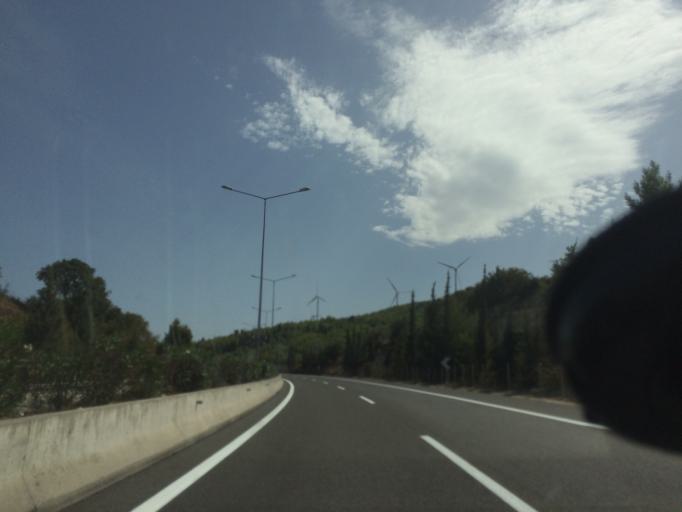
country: GR
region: Central Greece
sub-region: Nomos Fthiotidos
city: Martinon
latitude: 38.6010
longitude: 23.1795
